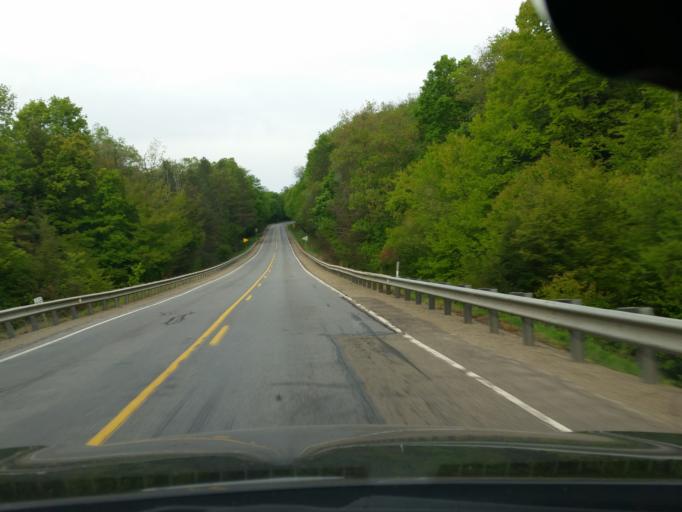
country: US
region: Pennsylvania
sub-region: McKean County
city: Kane
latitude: 41.5416
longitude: -78.7879
